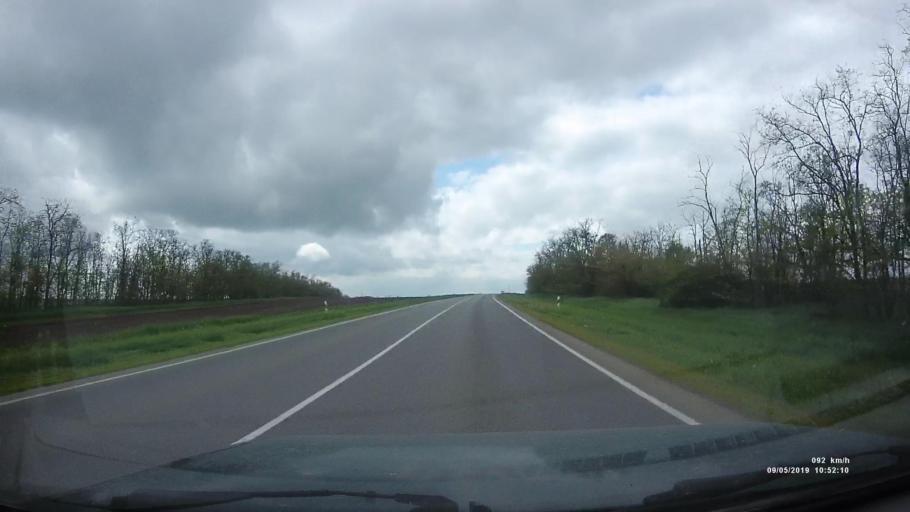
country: RU
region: Rostov
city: Peshkovo
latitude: 46.9044
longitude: 39.3546
